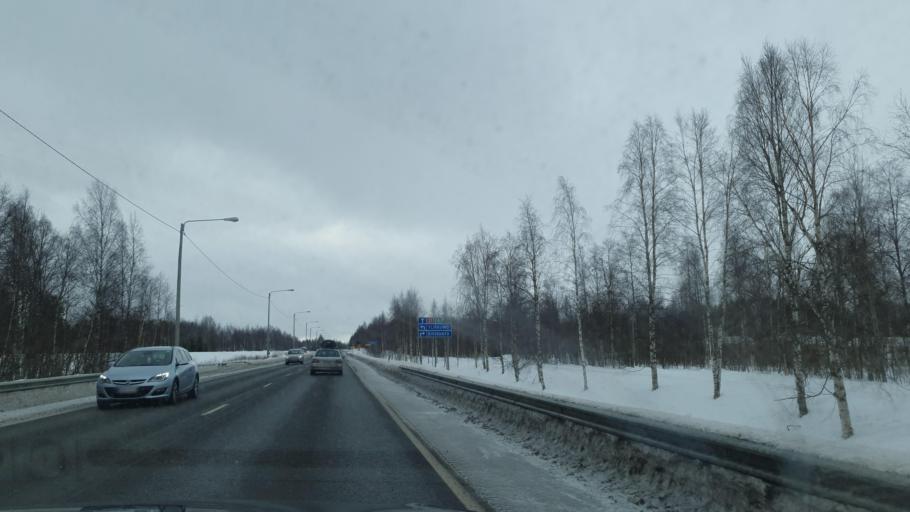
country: FI
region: Lapland
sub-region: Kemi-Tornio
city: Tornio
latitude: 65.8680
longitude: 24.1678
